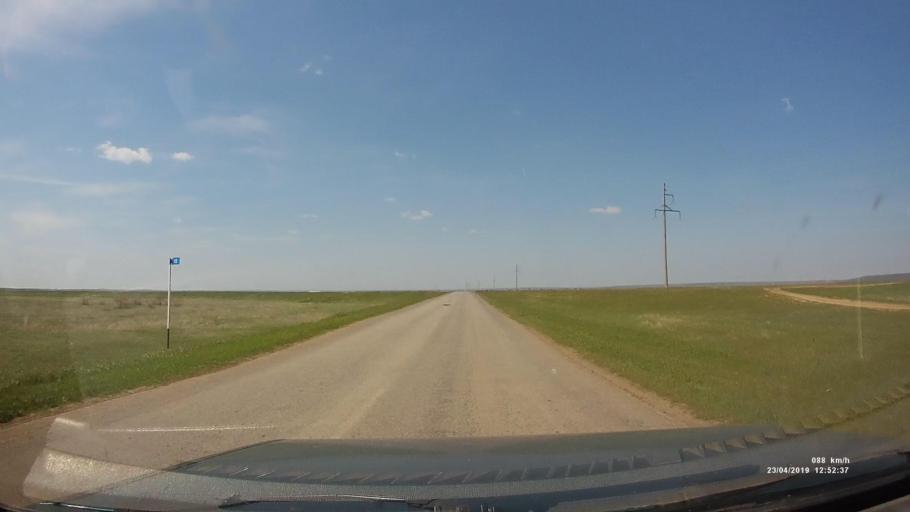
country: RU
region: Kalmykiya
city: Yashalta
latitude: 46.5664
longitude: 42.6071
